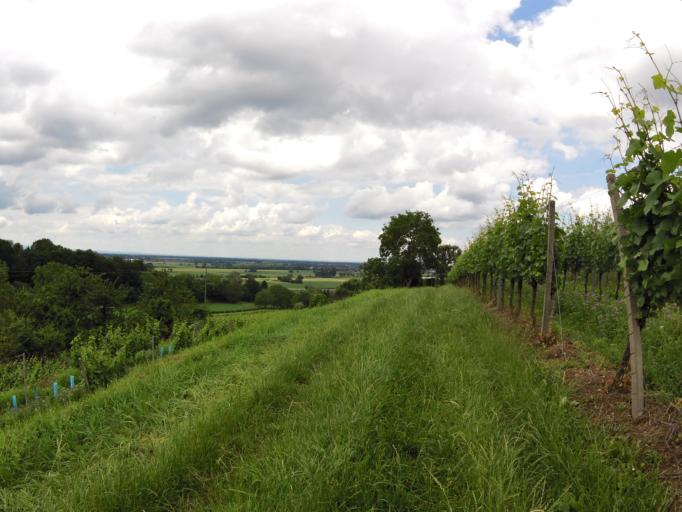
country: DE
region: Baden-Wuerttemberg
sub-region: Freiburg Region
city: Lahr
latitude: 48.3557
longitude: 7.8605
